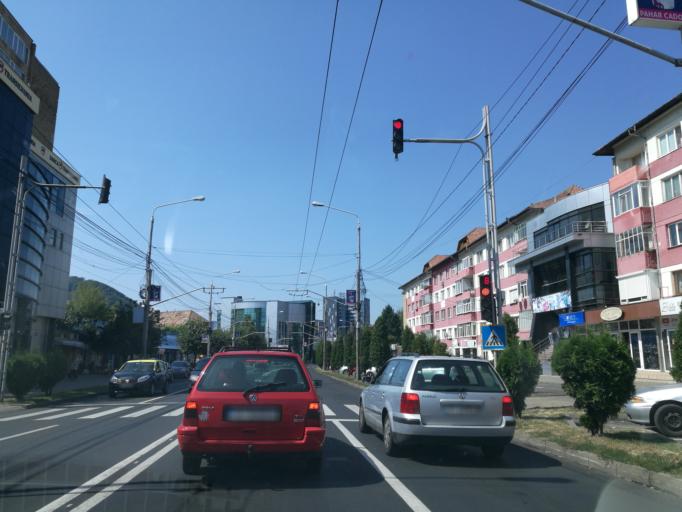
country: RO
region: Neamt
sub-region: Municipiul Piatra-Neamt
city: Valeni
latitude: 46.9285
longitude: 26.3679
